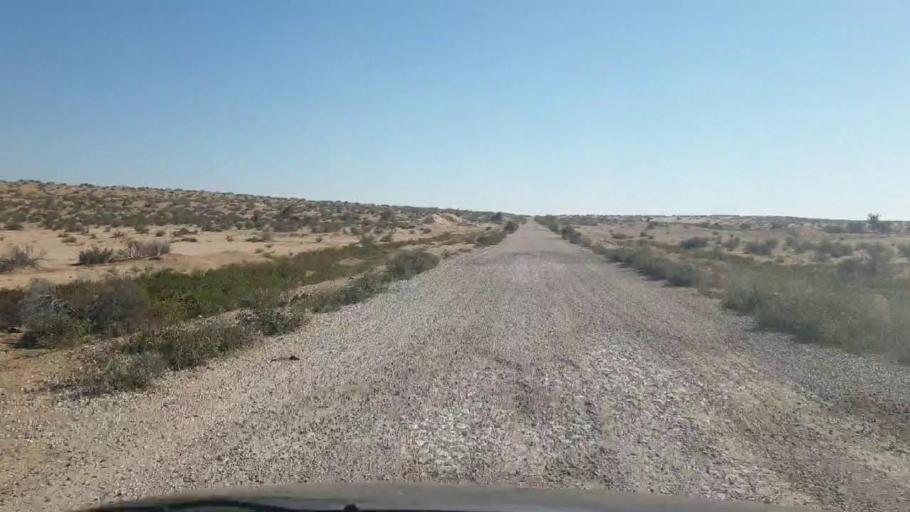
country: PK
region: Sindh
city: Bozdar
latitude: 27.0078
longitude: 68.8005
